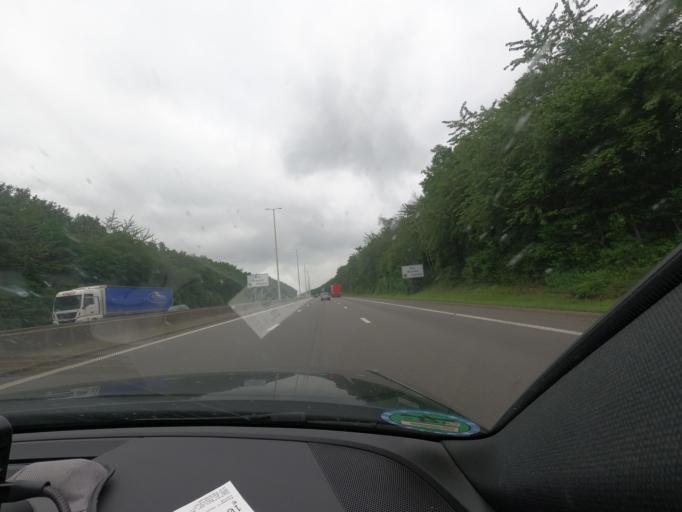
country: BE
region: Wallonia
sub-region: Province de Liege
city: Wanze
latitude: 50.5697
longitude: 5.1869
